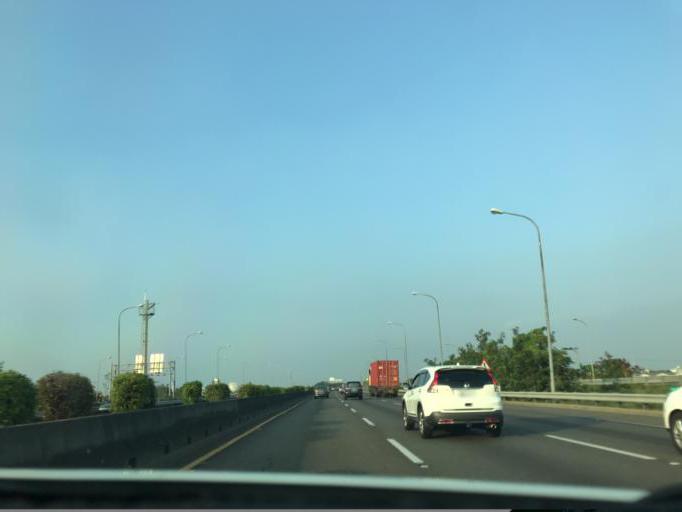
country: TW
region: Taiwan
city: Xinying
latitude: 23.2210
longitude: 120.2397
